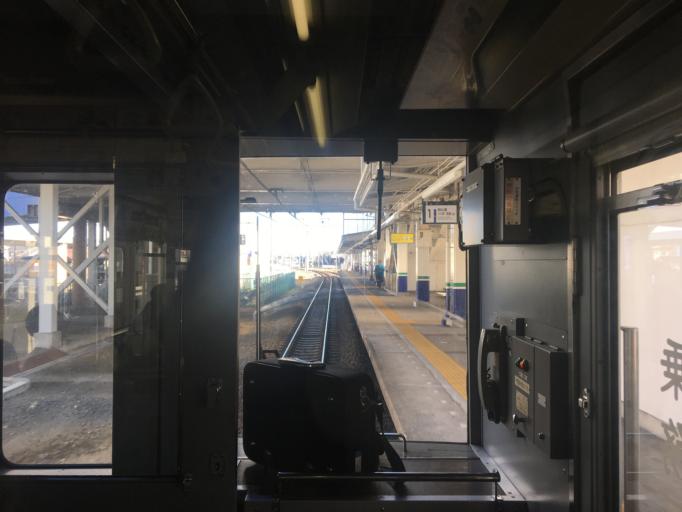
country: JP
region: Saitama
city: Sakado
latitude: 35.9712
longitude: 139.3961
